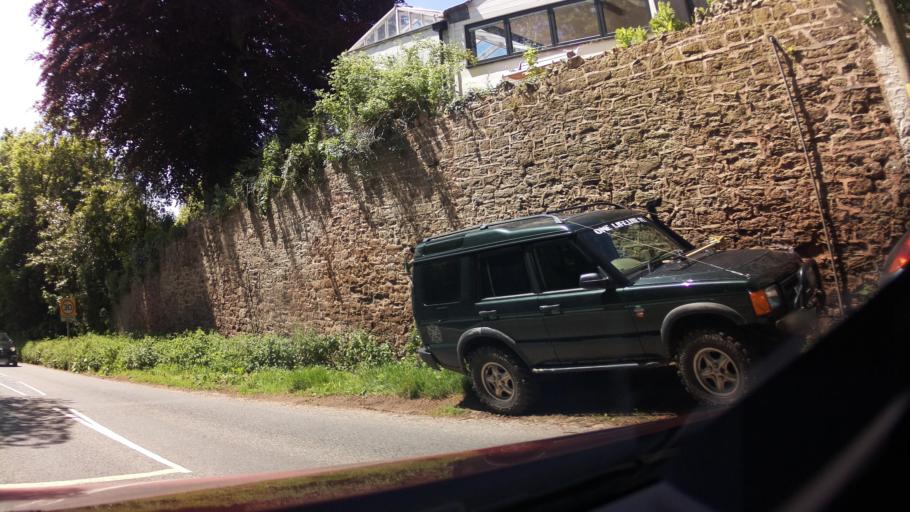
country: GB
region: England
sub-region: Devon
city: Budleigh Salterton
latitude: 50.6537
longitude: -3.3165
